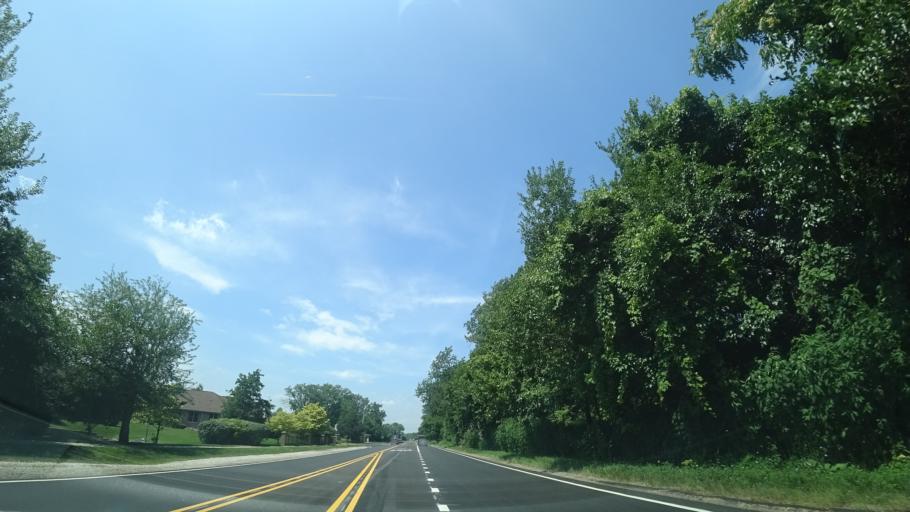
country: US
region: Illinois
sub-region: Cook County
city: Crestwood
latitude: 41.6701
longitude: -87.7728
